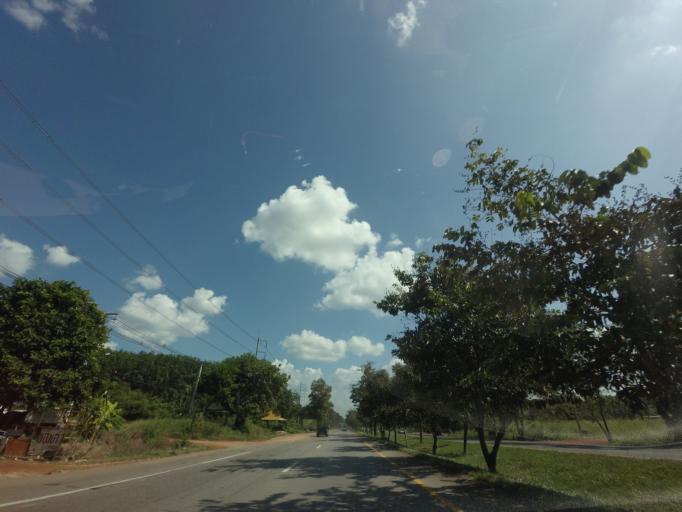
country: TH
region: Rayong
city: Wang Chan
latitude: 12.9540
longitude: 101.5095
